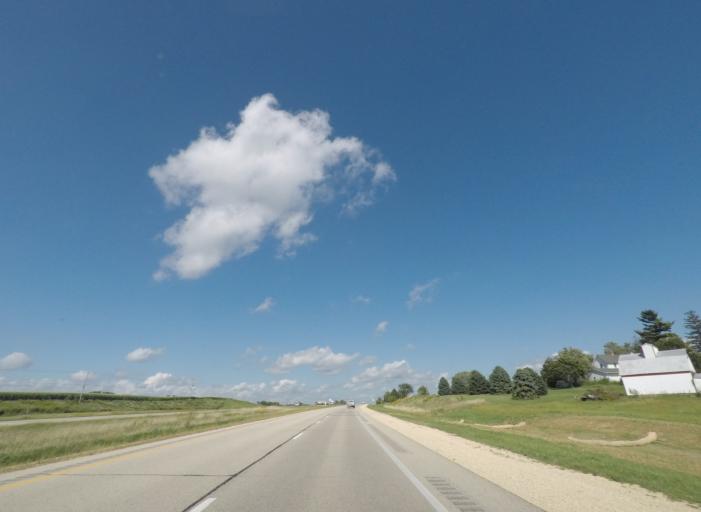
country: US
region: Iowa
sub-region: Dubuque County
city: Peosta
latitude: 42.3975
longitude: -90.7566
